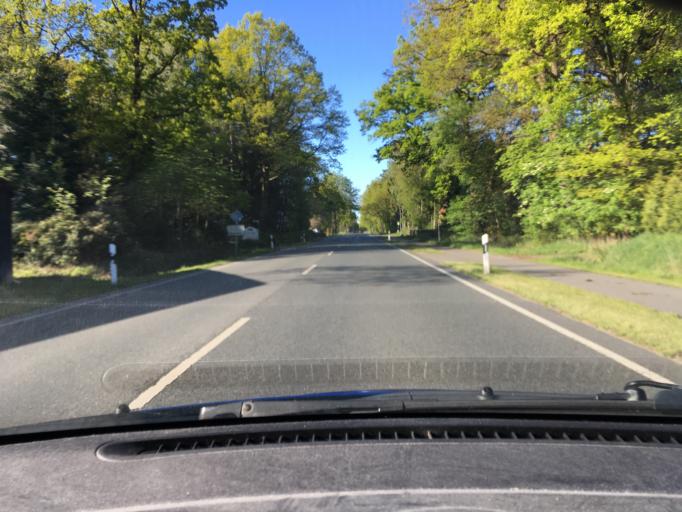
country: DE
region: Lower Saxony
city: Soltau
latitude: 53.0387
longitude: 9.8545
